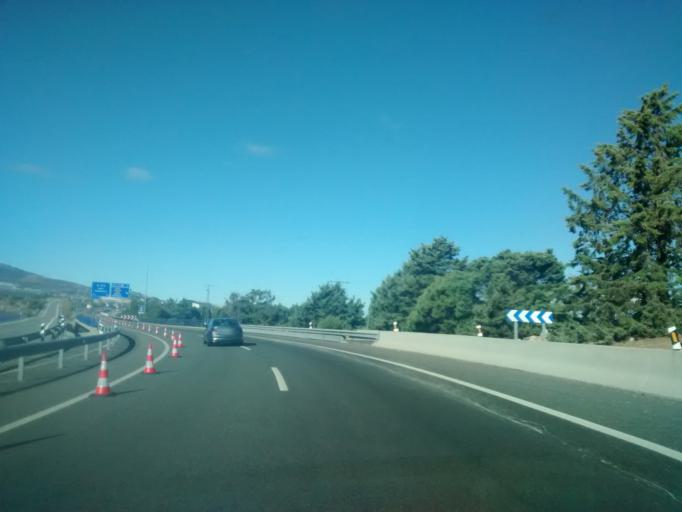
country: ES
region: Castille and Leon
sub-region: Provincia de Segovia
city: Villacastin
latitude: 40.7749
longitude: -4.4181
